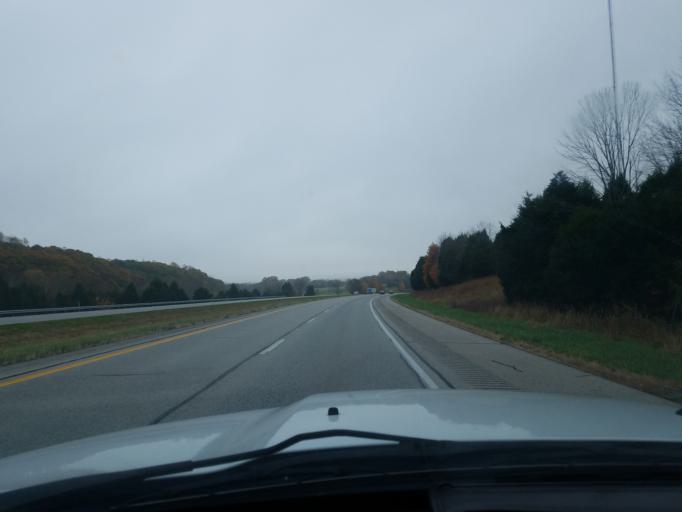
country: US
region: Indiana
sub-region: Harrison County
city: Corydon
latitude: 38.2445
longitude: -86.0930
